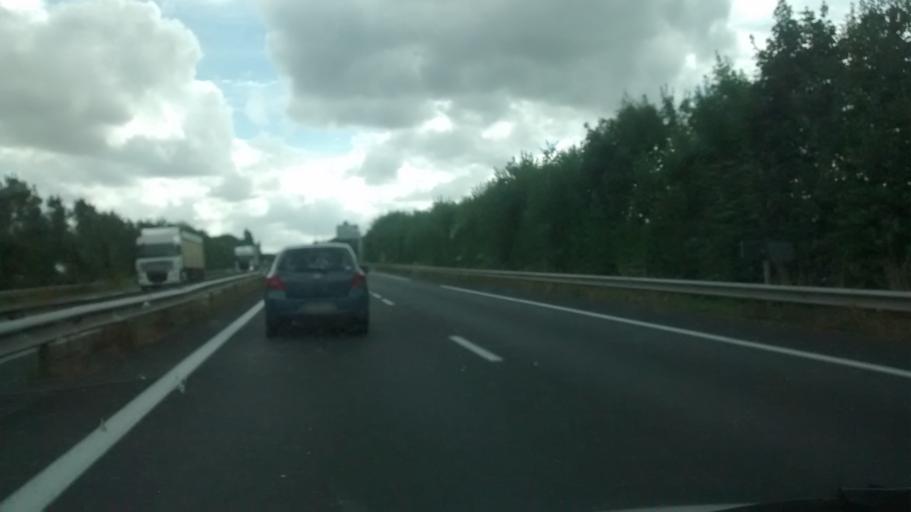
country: FR
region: Lower Normandy
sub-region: Departement du Calvados
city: Grainville-sur-Odon
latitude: 49.1140
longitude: -0.5889
